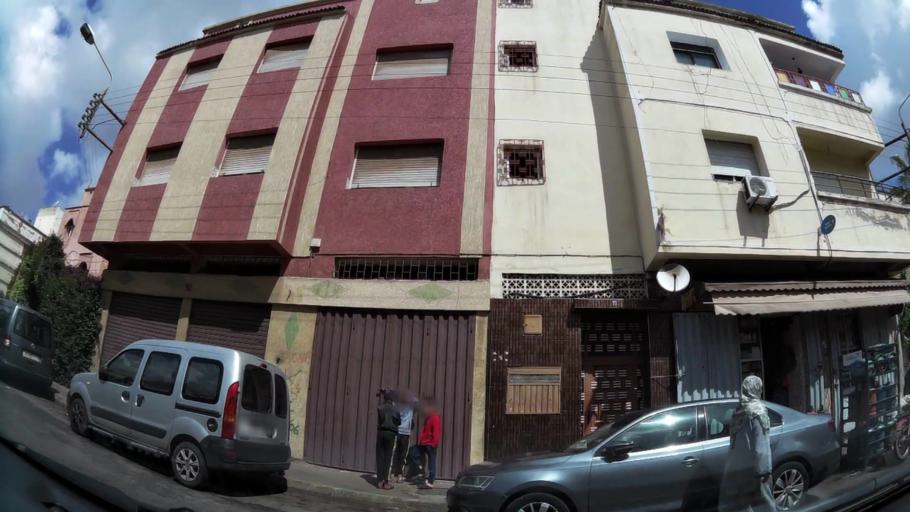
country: MA
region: Grand Casablanca
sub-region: Casablanca
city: Casablanca
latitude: 33.5411
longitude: -7.5867
